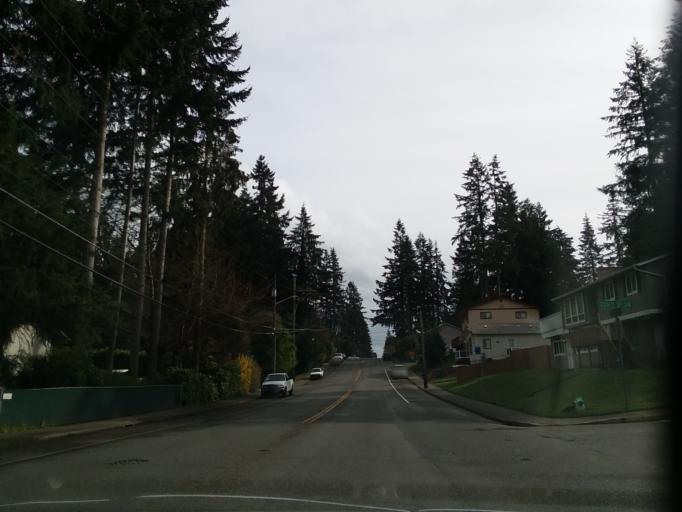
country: US
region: Washington
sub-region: Snohomish County
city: Mountlake Terrace
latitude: 47.7941
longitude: -122.3220
